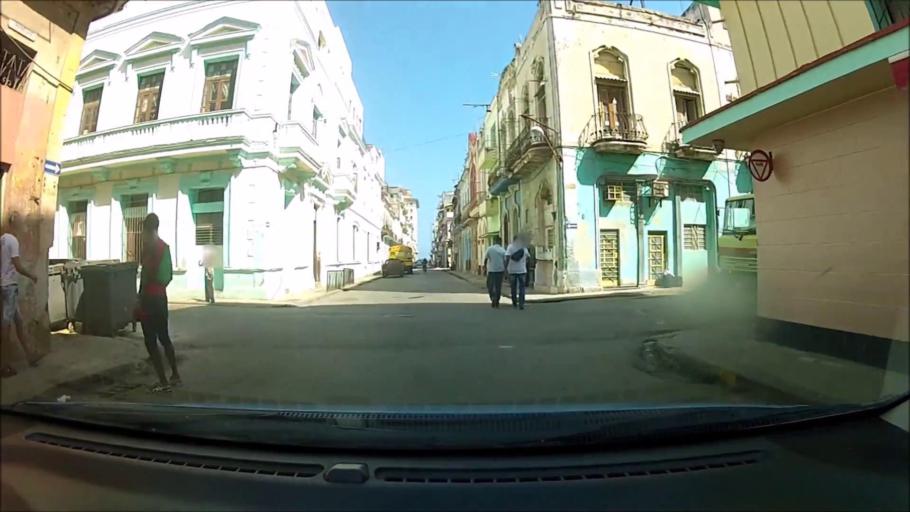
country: CU
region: La Habana
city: Centro Habana
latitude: 23.1384
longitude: -82.3661
